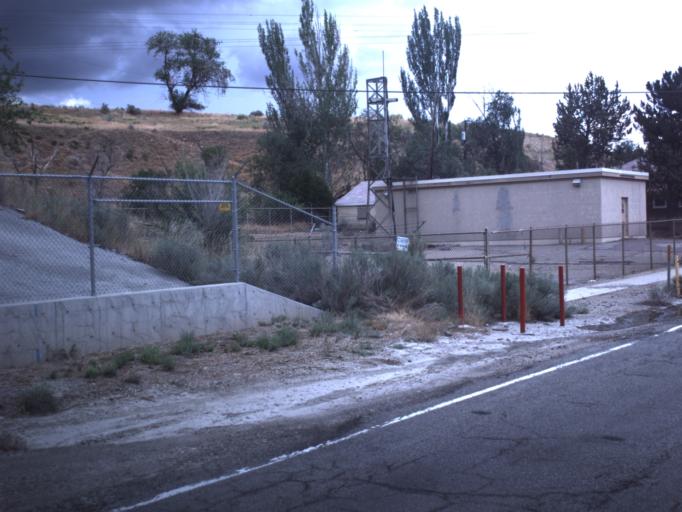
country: US
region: Utah
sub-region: Salt Lake County
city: Herriman
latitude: 40.5638
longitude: -112.1054
